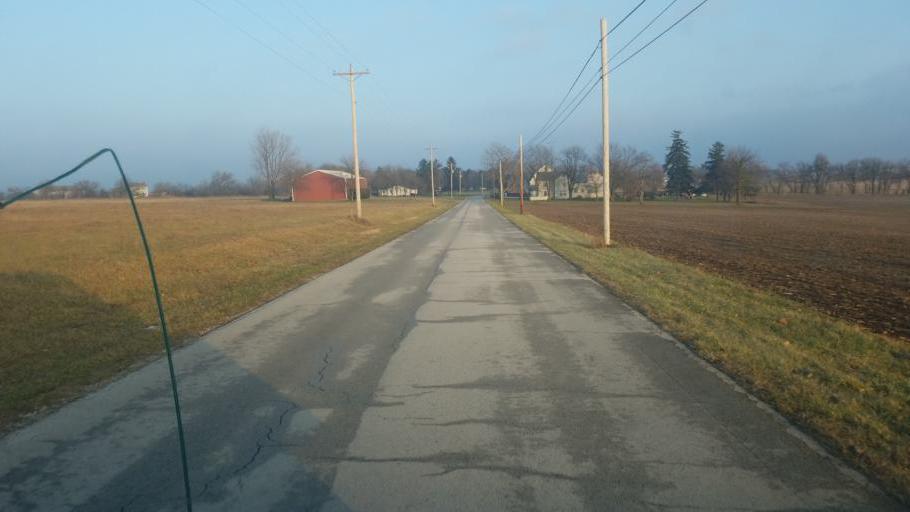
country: US
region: Ohio
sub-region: Wyandot County
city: Carey
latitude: 40.9620
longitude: -83.4280
